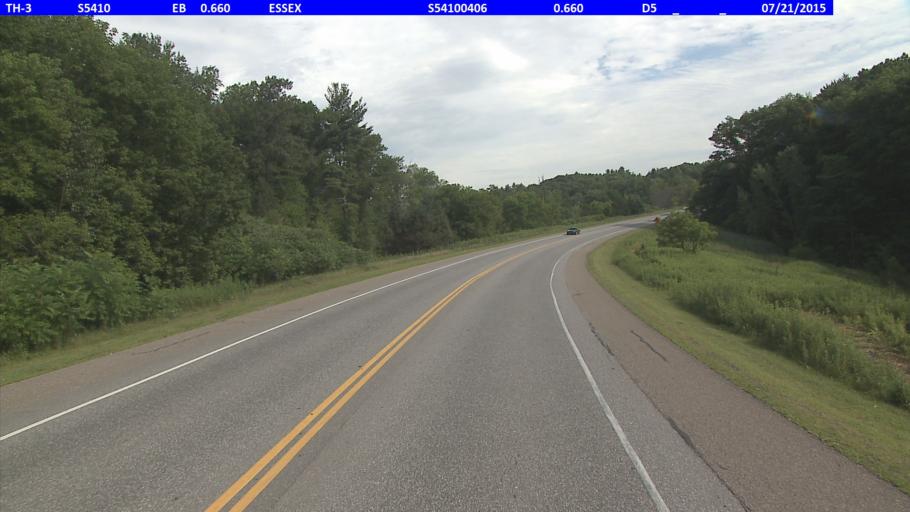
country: US
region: Vermont
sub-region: Chittenden County
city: Essex Junction
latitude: 44.5123
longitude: -73.1317
